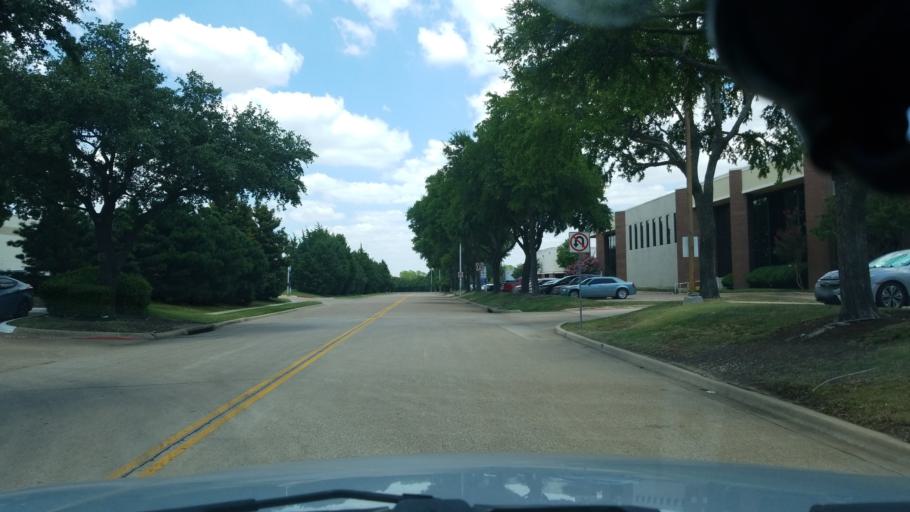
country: US
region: Texas
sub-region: Dallas County
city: Duncanville
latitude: 32.6798
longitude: -96.8802
